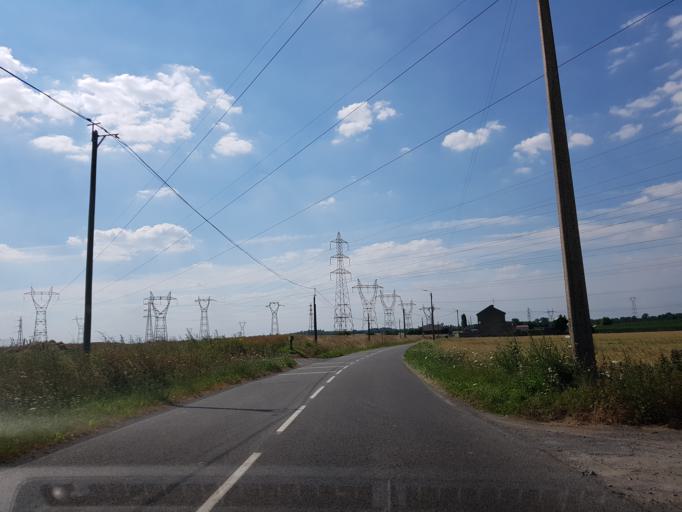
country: FR
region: Nord-Pas-de-Calais
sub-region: Departement du Nord
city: Roeulx
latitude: 50.3150
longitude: 3.3300
